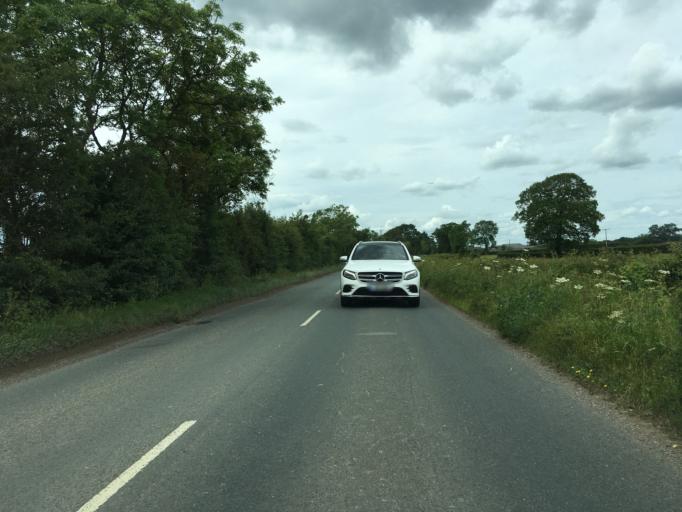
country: GB
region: England
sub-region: Wiltshire
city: Royal Wootton Bassett
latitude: 51.5604
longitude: -1.9261
